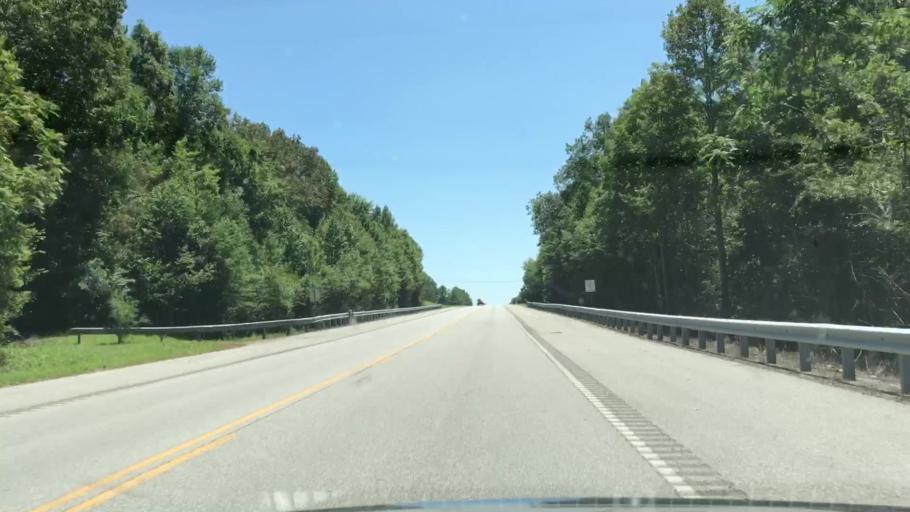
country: US
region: Tennessee
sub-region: Putnam County
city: Baxter
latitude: 36.2214
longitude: -85.6155
